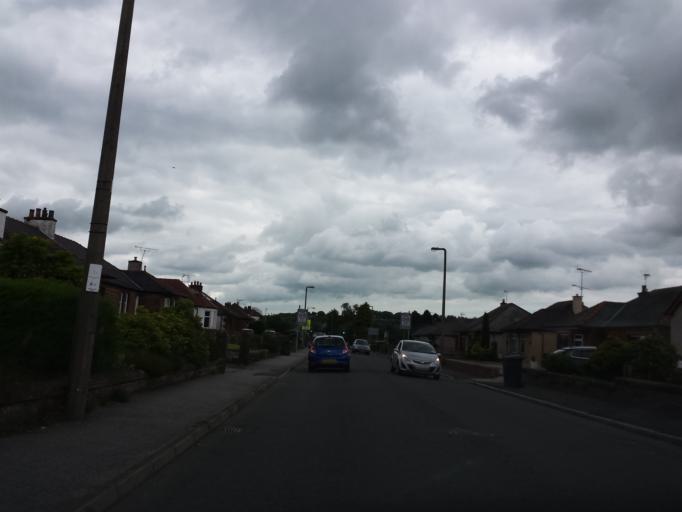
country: GB
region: Scotland
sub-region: Dumfries and Galloway
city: Dumfries
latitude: 55.0611
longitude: -3.6204
